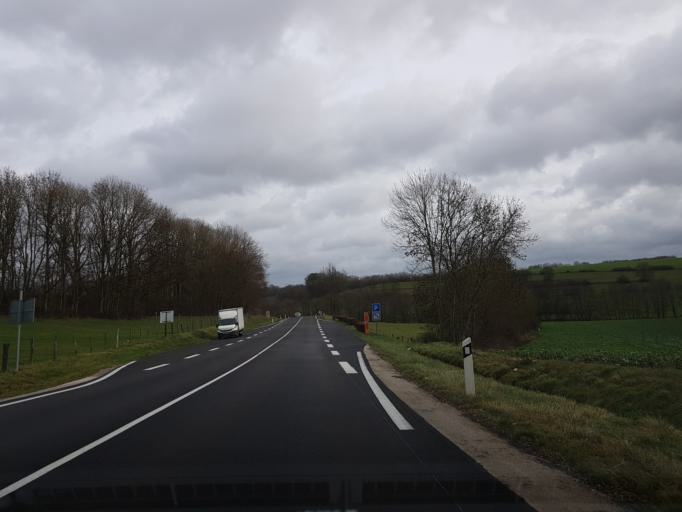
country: FR
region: Champagne-Ardenne
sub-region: Departement de la Haute-Marne
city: Langres
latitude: 47.8576
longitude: 5.3587
